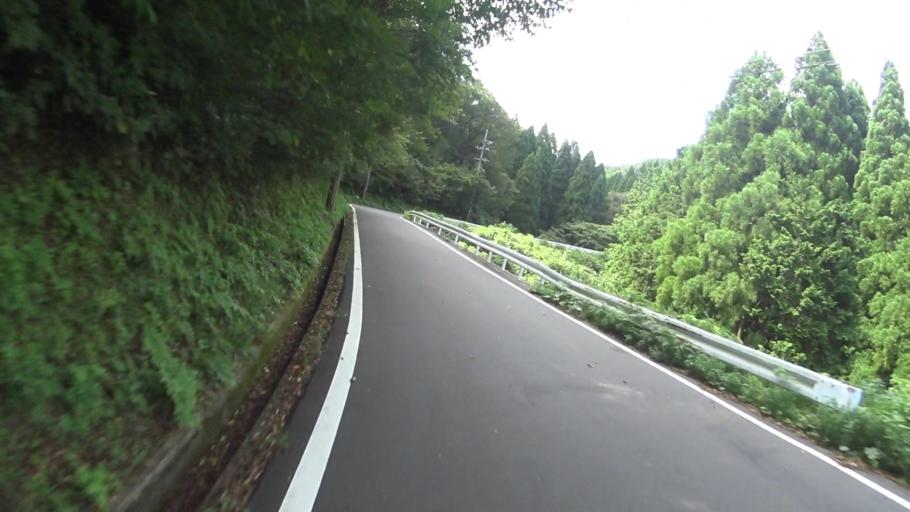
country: JP
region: Kyoto
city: Miyazu
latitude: 35.7287
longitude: 135.2053
